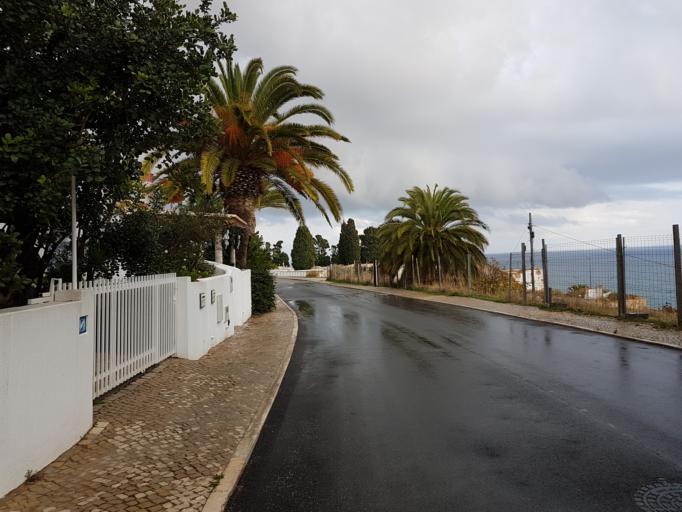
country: PT
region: Faro
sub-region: Albufeira
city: Albufeira
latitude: 37.0842
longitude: -8.2605
